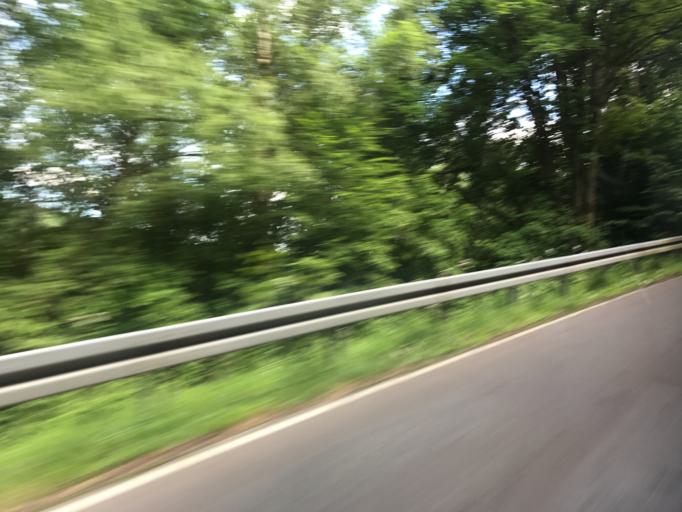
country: DE
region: Hesse
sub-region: Regierungsbezirk Darmstadt
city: Schlangenbad
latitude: 50.0701
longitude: 8.1090
